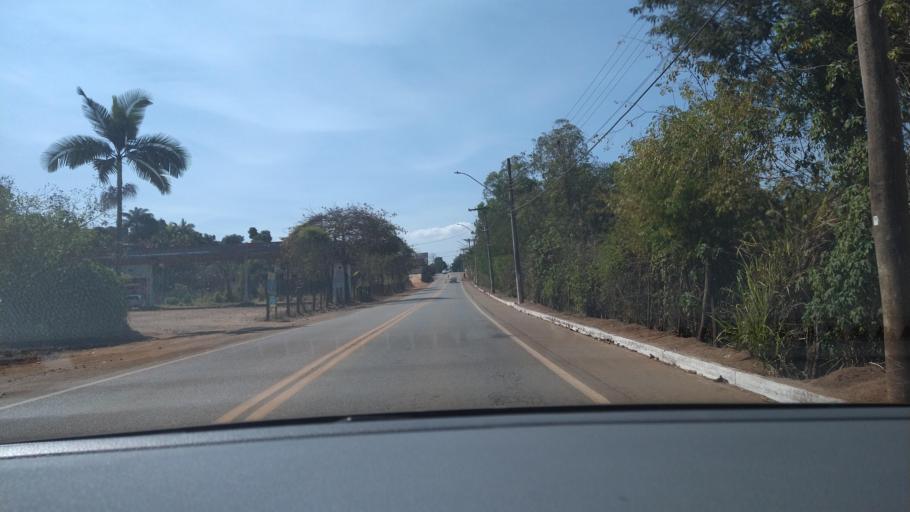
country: BR
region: Minas Gerais
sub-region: Rio Piracicaba
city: Rio Piracicaba
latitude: -19.9216
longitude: -43.1628
